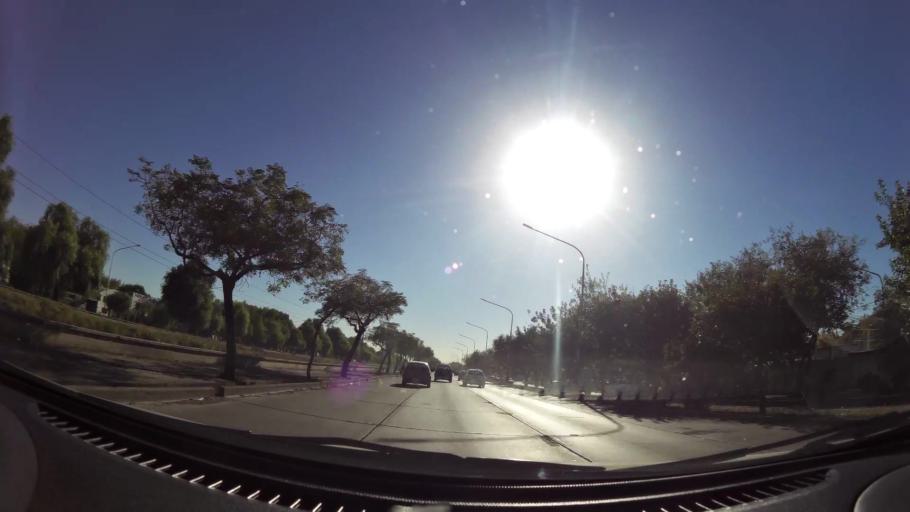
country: AR
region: Mendoza
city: Mendoza
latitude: -32.8752
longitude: -68.8227
